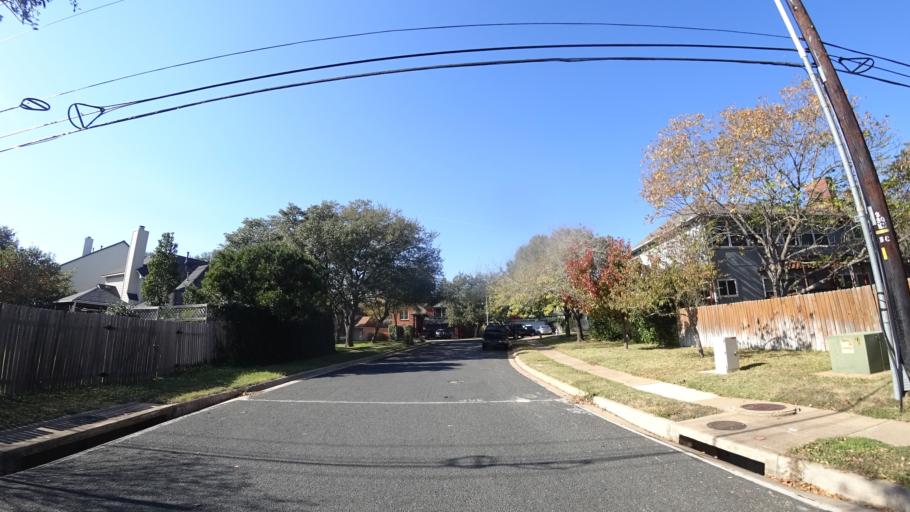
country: US
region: Texas
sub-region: Travis County
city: Shady Hollow
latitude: 30.2226
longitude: -97.8680
